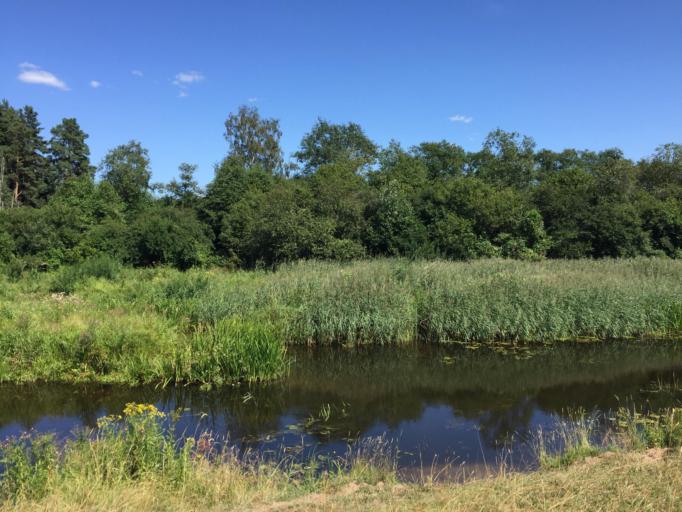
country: LV
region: Kandava
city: Kandava
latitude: 57.0157
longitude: 22.7029
